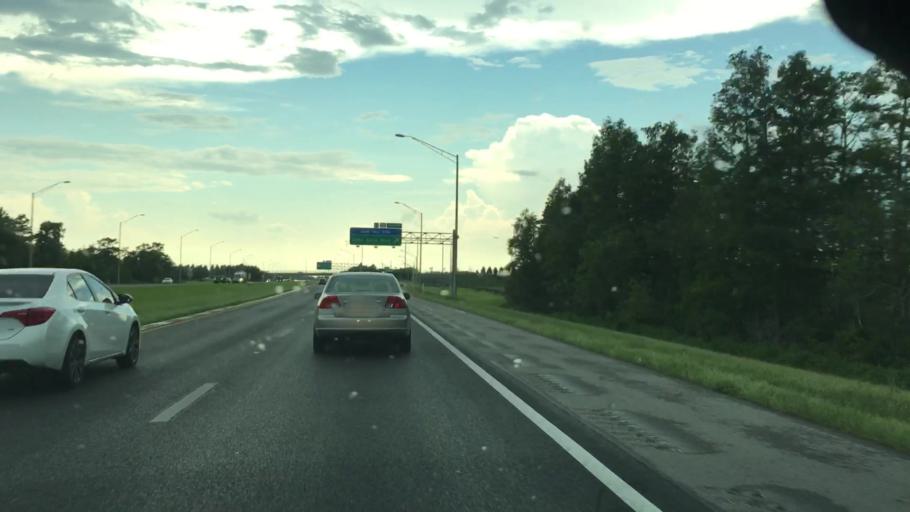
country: US
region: Florida
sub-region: Osceola County
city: Buenaventura Lakes
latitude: 28.3824
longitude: -81.2693
